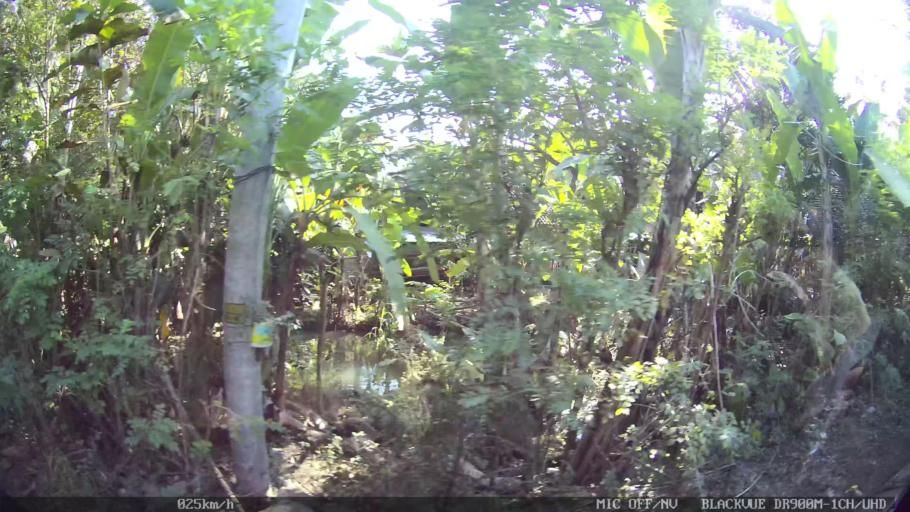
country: ID
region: Daerah Istimewa Yogyakarta
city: Kasihan
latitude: -7.8355
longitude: 110.2854
